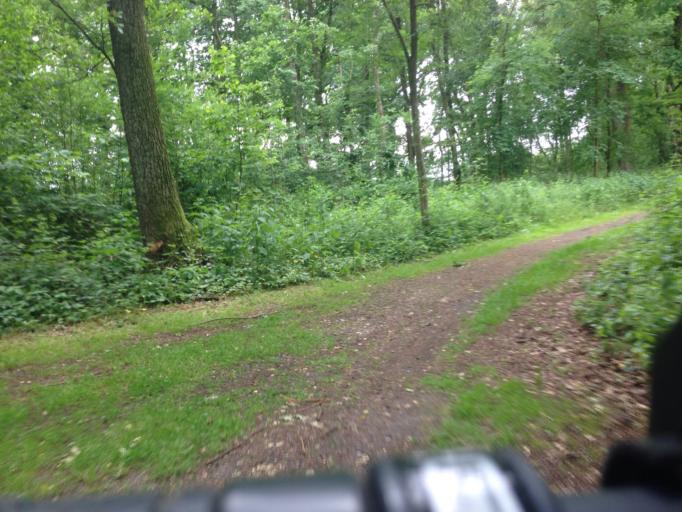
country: DE
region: Schleswig-Holstein
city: Barsbuettel
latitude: 53.5861
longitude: 10.1668
